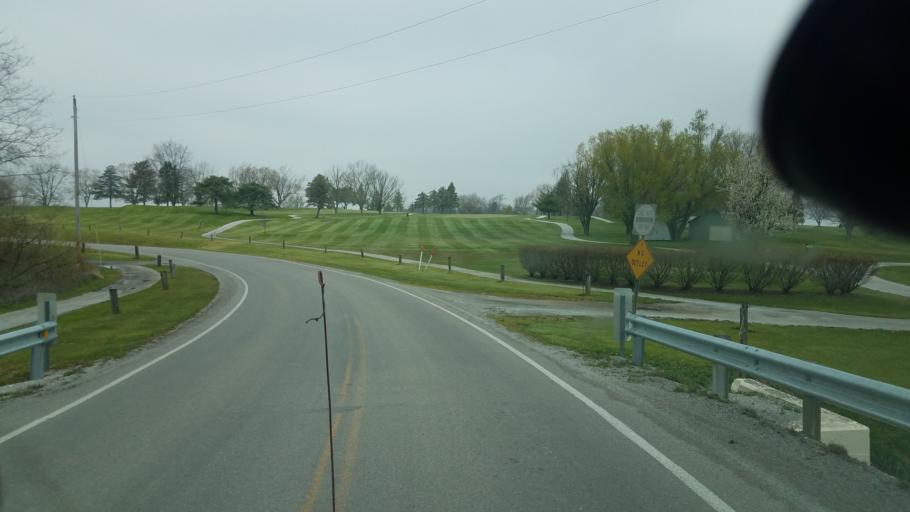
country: US
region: Ohio
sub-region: Hardin County
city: Kenton
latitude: 40.6386
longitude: -83.5745
